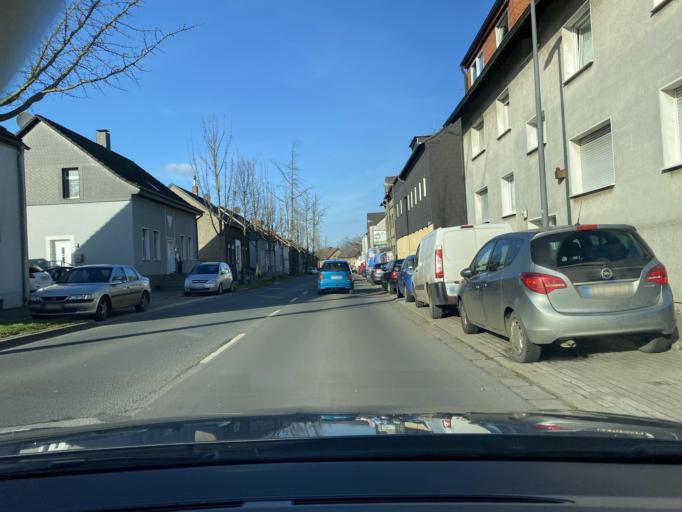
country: DE
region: North Rhine-Westphalia
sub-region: Regierungsbezirk Dusseldorf
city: Essen
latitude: 51.5060
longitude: 7.0492
